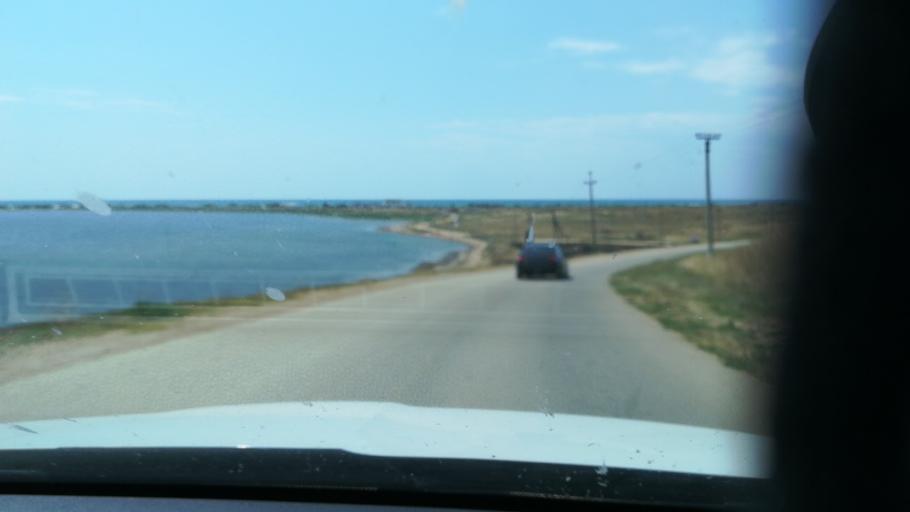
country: RU
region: Krasnodarskiy
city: Vyshestebliyevskaya
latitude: 45.1167
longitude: 36.8945
